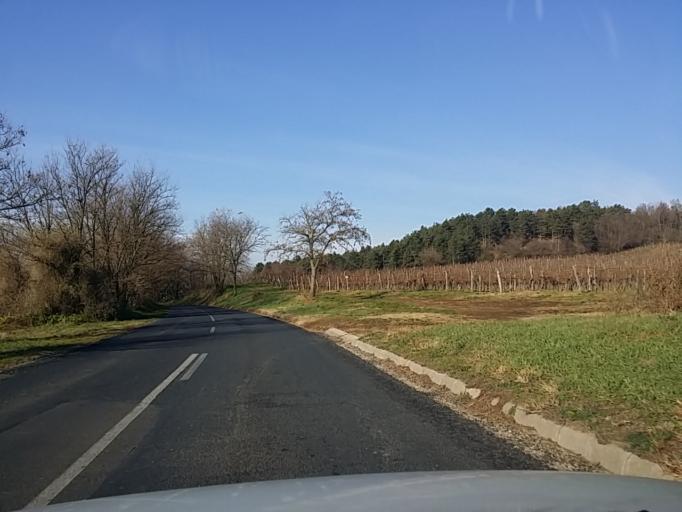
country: HU
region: Veszprem
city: Badacsonytomaj
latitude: 46.8614
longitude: 17.4992
